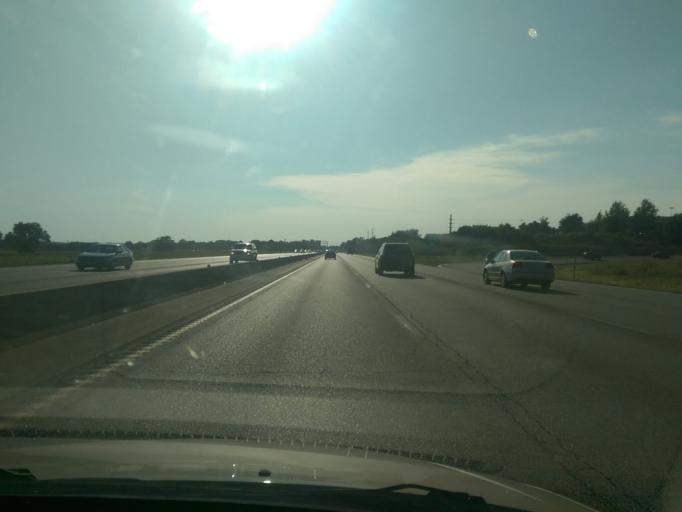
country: US
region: Missouri
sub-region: Jackson County
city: East Independence
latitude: 39.0420
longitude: -94.3633
